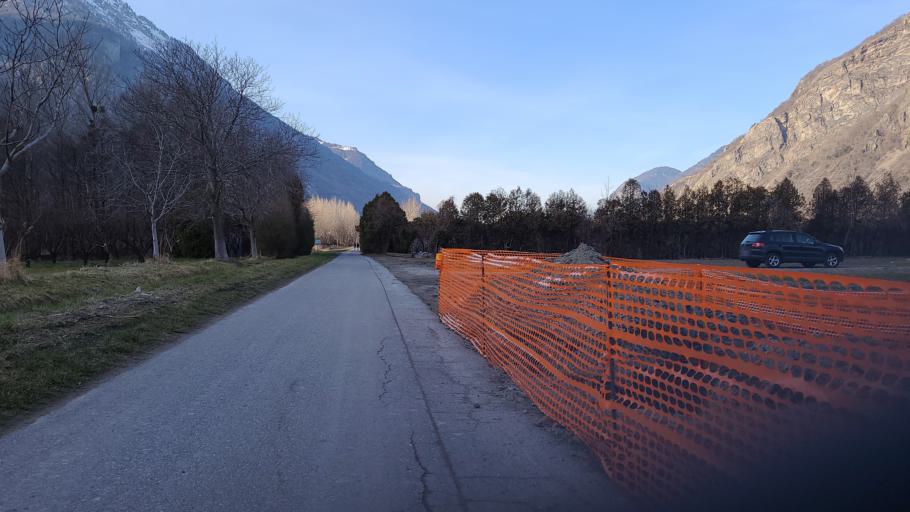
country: CH
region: Valais
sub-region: Saint-Maurice District
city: Vernayaz
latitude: 46.1264
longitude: 7.0522
